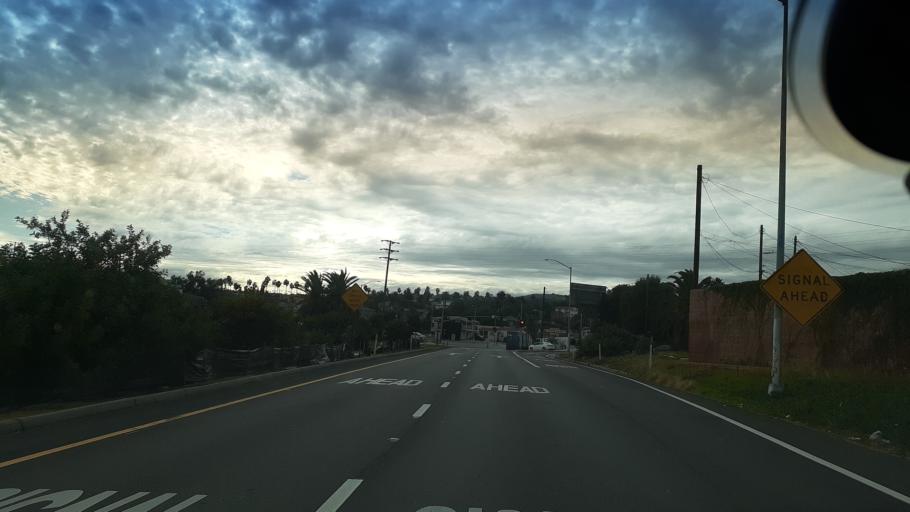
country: US
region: California
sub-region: Los Angeles County
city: San Pedro
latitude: 33.7484
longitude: -118.2914
